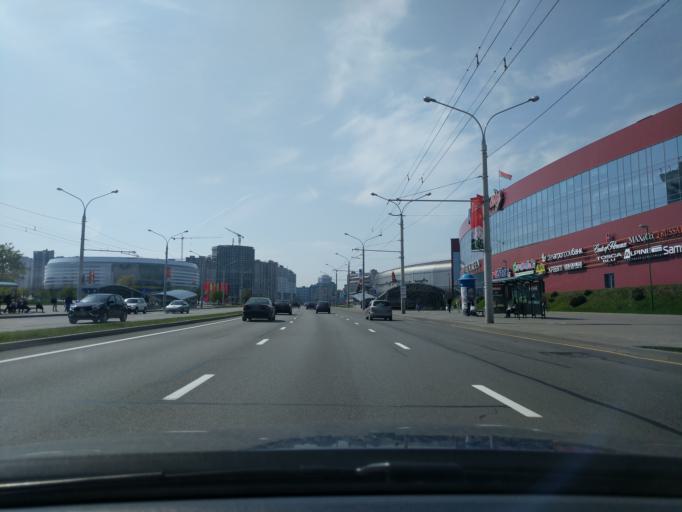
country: BY
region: Minsk
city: Zhdanovichy
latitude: 53.9374
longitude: 27.4892
